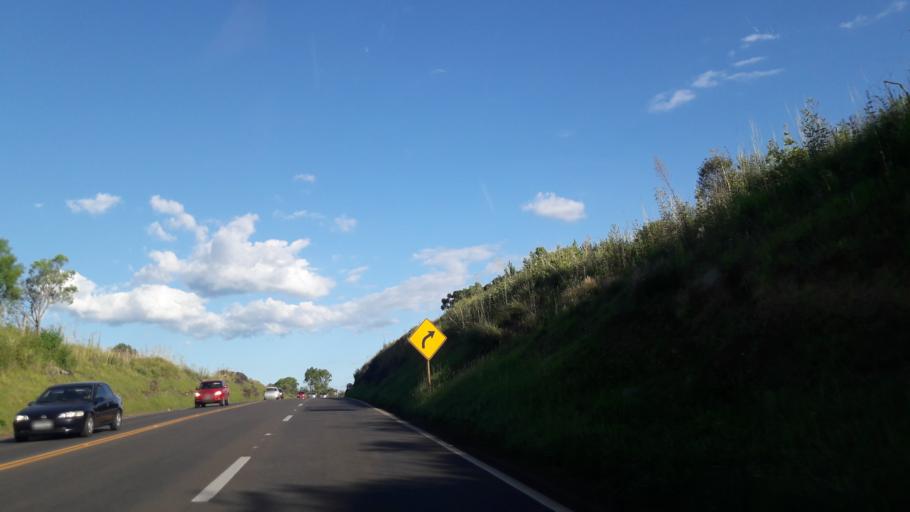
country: BR
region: Parana
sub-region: Guarapuava
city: Guarapuava
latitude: -25.3592
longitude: -51.3556
